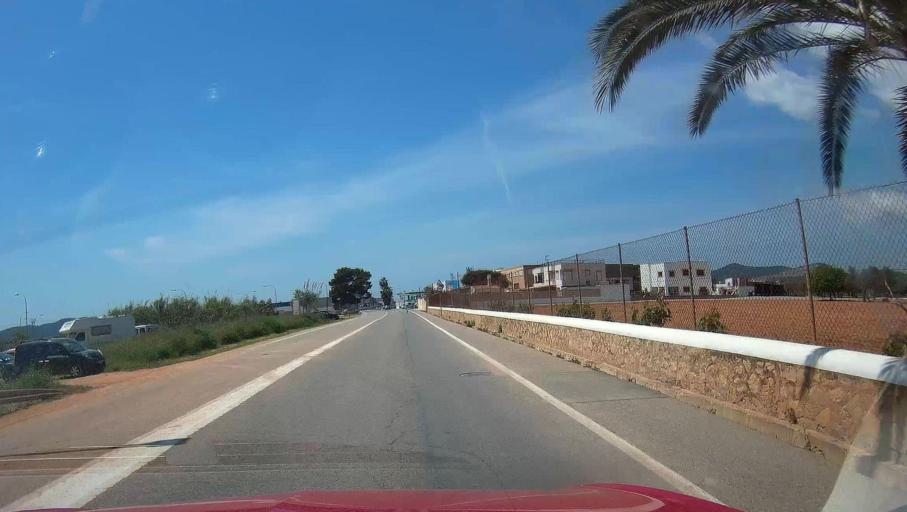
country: ES
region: Balearic Islands
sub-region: Illes Balears
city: Ibiza
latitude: 38.8874
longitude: 1.3946
